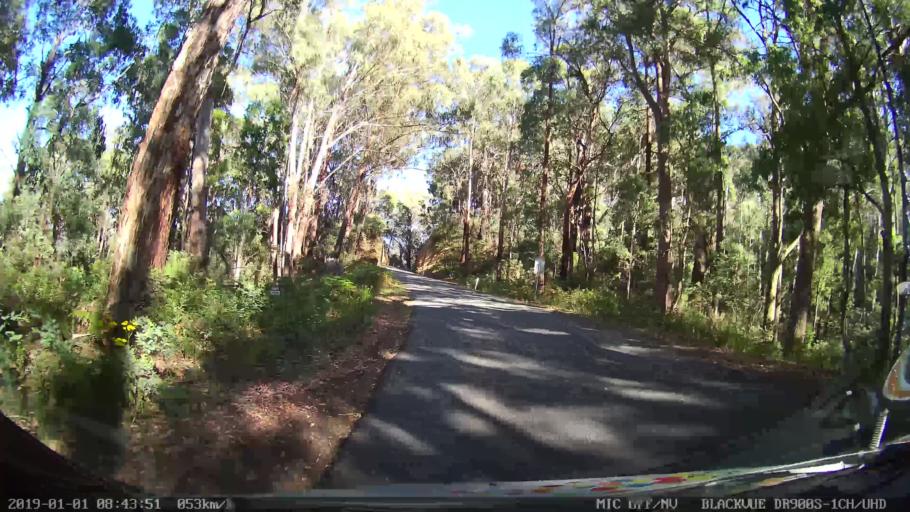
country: AU
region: New South Wales
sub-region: Snowy River
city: Jindabyne
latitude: -36.3142
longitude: 148.1917
